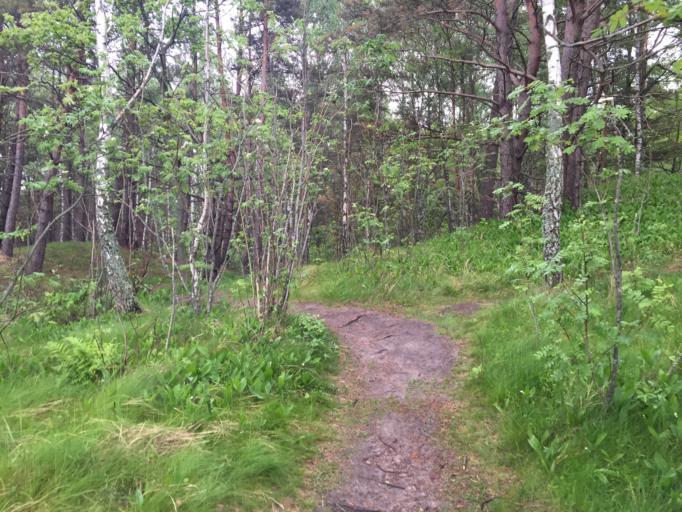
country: LT
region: Klaipedos apskritis
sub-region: Klaipeda
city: Klaipeda
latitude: 55.7968
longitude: 21.0678
